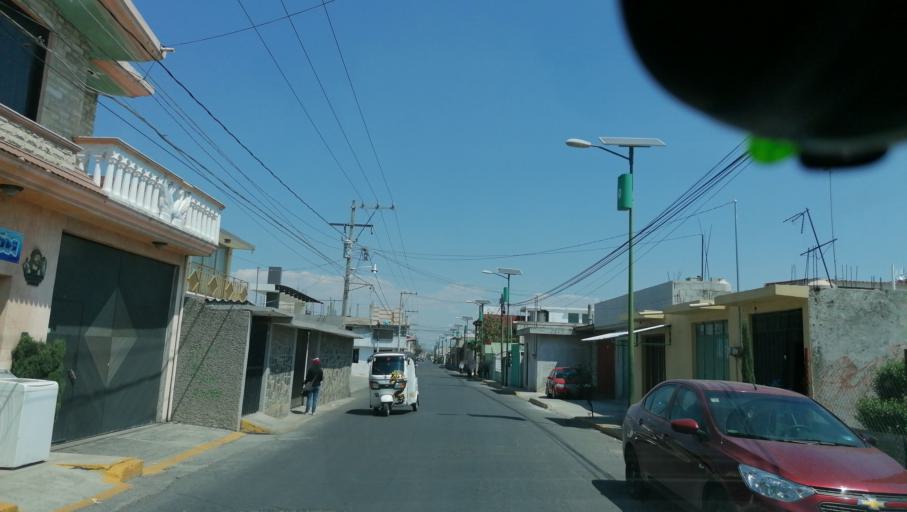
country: MX
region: Puebla
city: Huejotzingo
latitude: 19.1610
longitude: -98.4122
